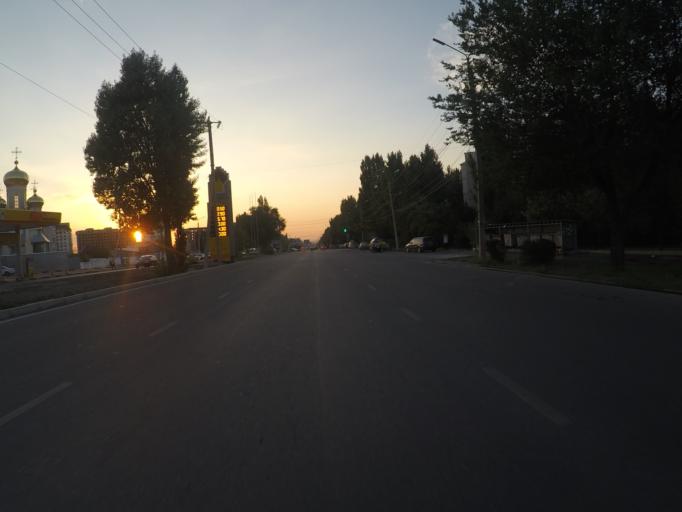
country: KG
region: Chuy
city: Bishkek
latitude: 42.8127
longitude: 74.6321
